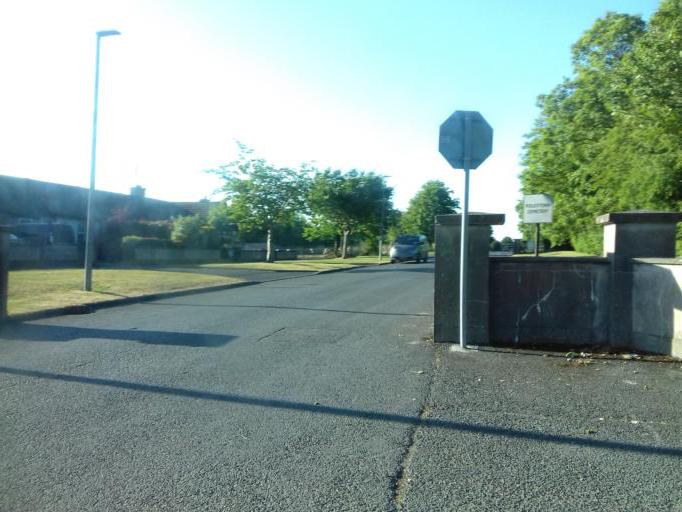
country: IE
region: Leinster
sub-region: Fingal County
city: Swords
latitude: 53.4901
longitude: -6.2987
